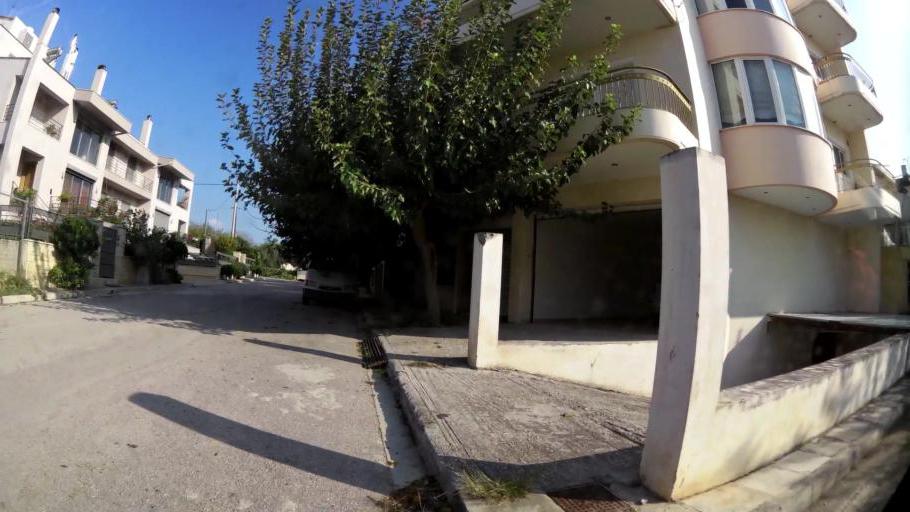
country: GR
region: Attica
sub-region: Nomarchia Athinas
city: Metamorfosi
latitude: 38.0575
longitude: 23.7422
